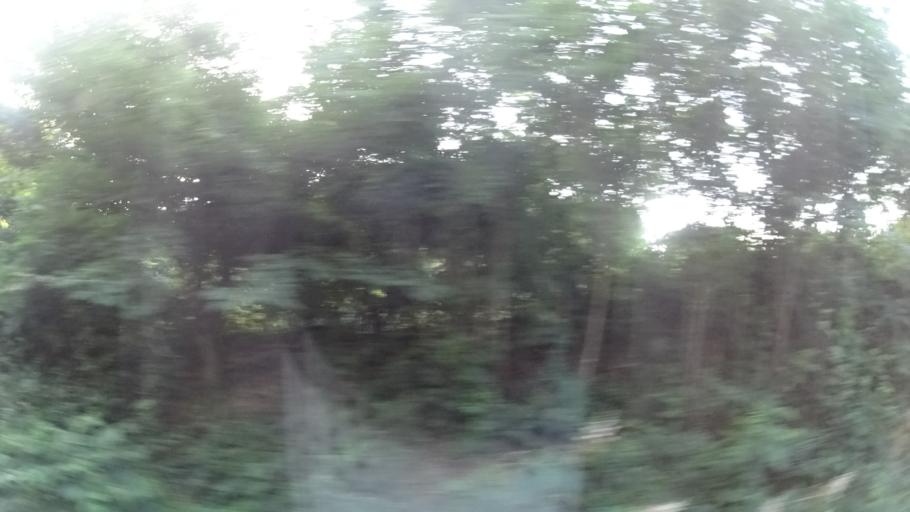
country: JP
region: Fukushima
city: Miharu
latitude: 37.4186
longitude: 140.4401
